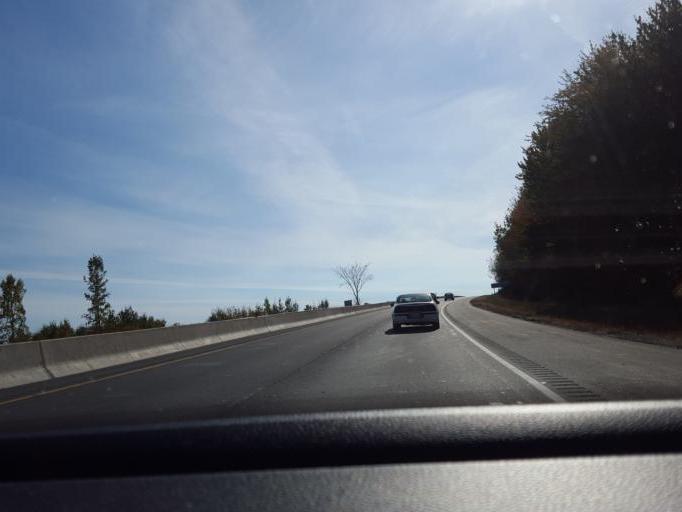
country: CA
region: Ontario
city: Oshawa
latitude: 43.9260
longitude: -78.6010
